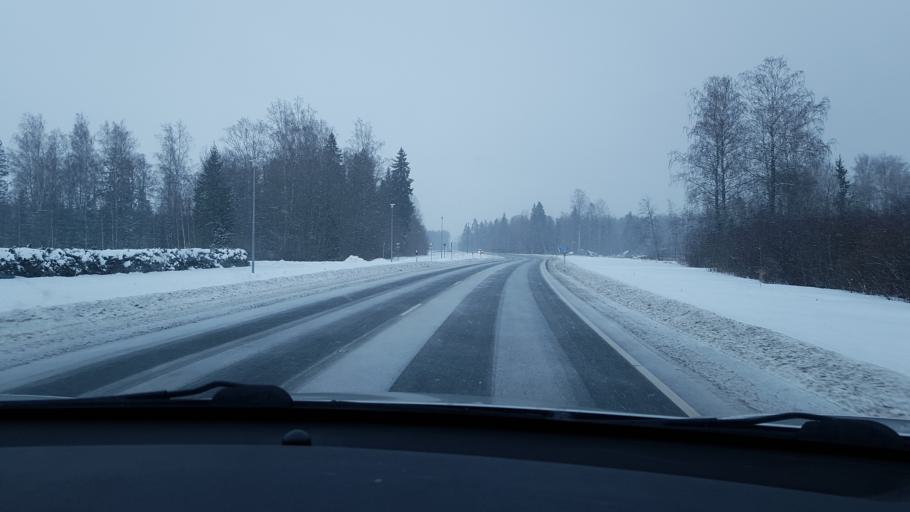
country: EE
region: Jaervamaa
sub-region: Tueri vald
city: Tueri
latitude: 58.8554
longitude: 25.4844
